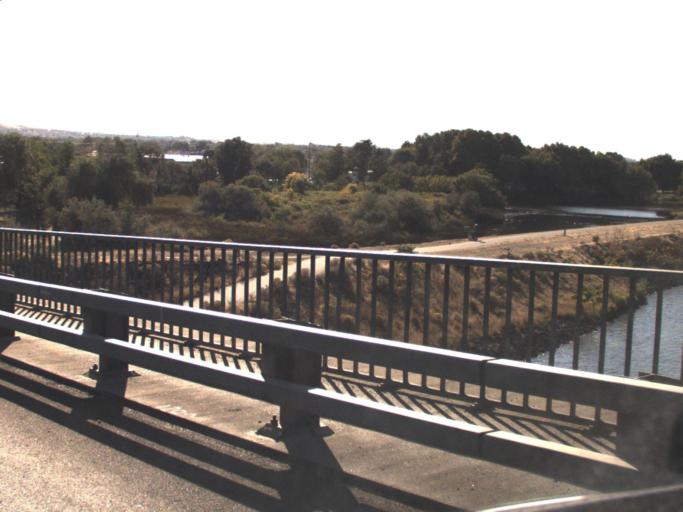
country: US
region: Washington
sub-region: Franklin County
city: Pasco
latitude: 46.2152
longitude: -119.1065
